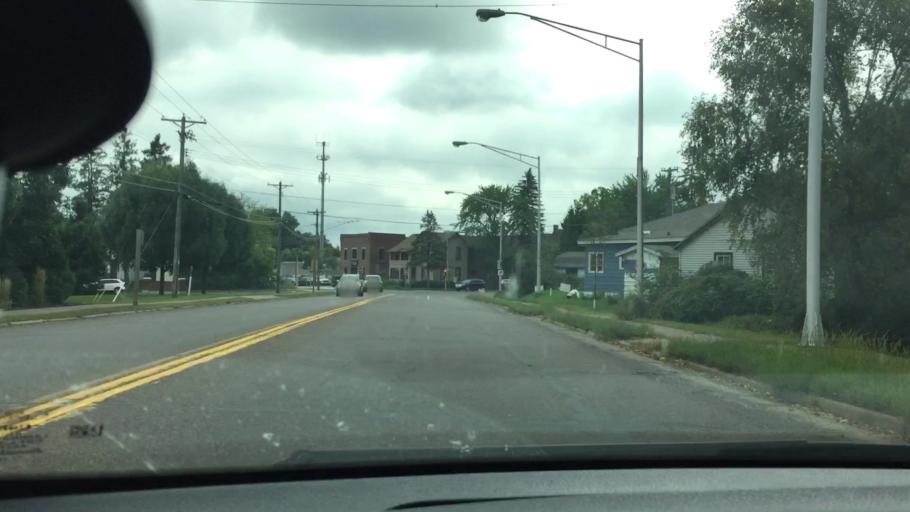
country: US
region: Wisconsin
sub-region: Chippewa County
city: Chippewa Falls
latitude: 44.9435
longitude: -91.3963
